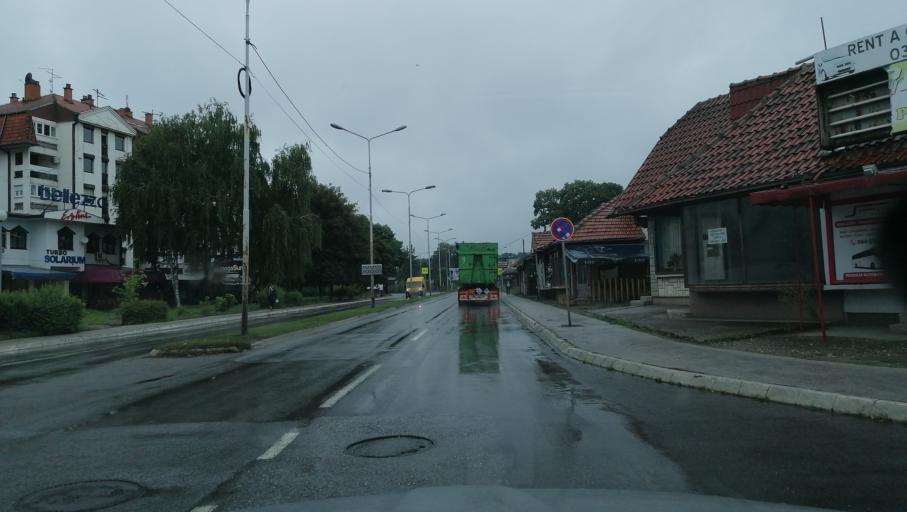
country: RS
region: Central Serbia
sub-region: Raski Okrug
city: Kraljevo
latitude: 43.7281
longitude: 20.6881
